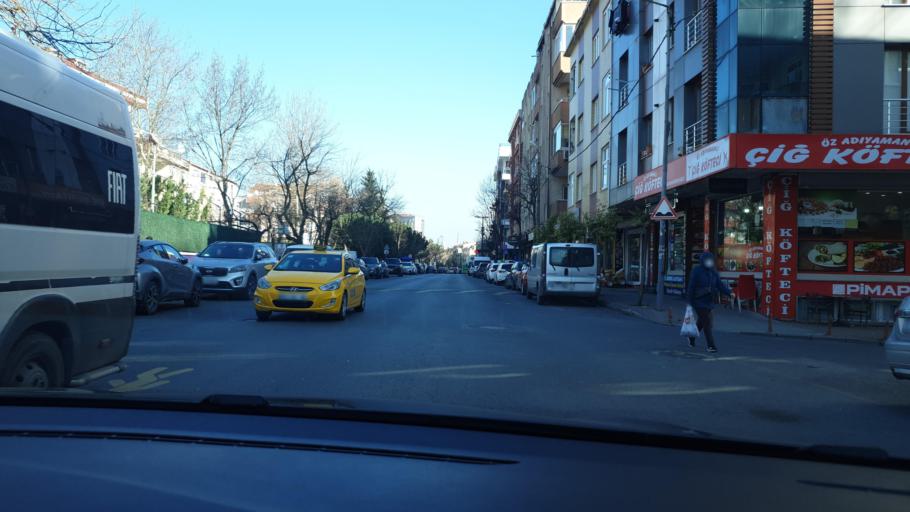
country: TR
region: Istanbul
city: Sisli
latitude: 41.0769
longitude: 28.9600
